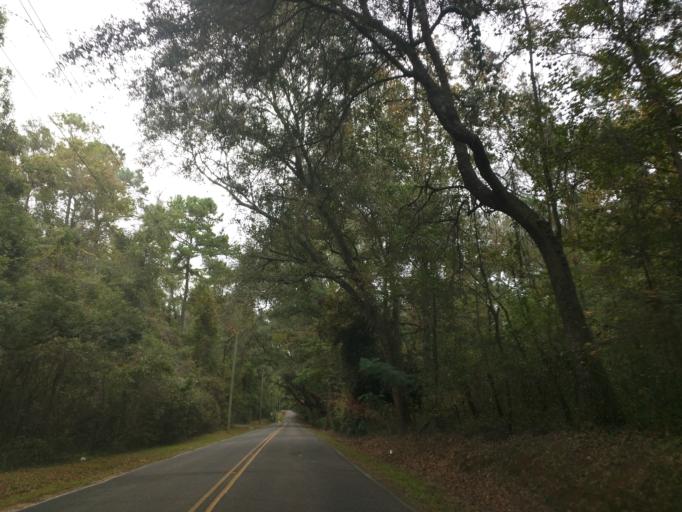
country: US
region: Florida
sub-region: Leon County
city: Tallahassee
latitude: 30.4224
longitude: -84.2101
